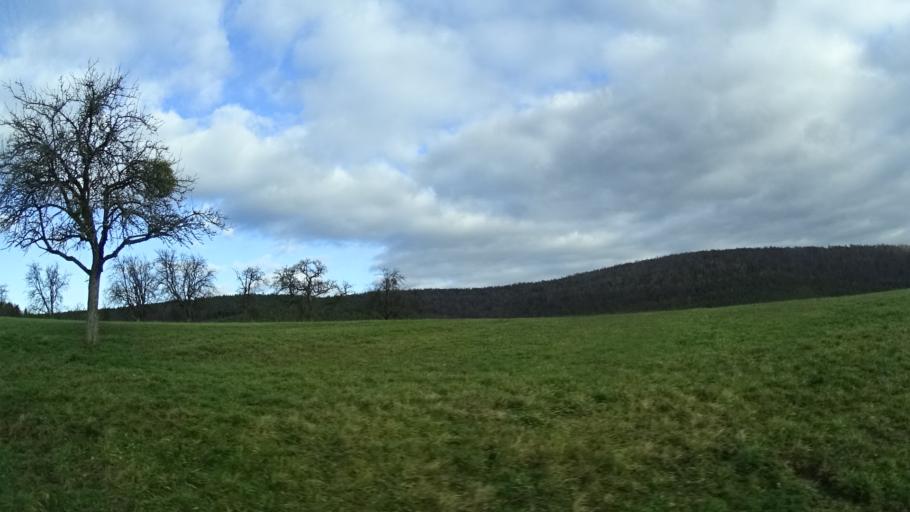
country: DE
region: Bavaria
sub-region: Regierungsbezirk Unterfranken
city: Neunkirchen
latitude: 49.8024
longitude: 9.4037
